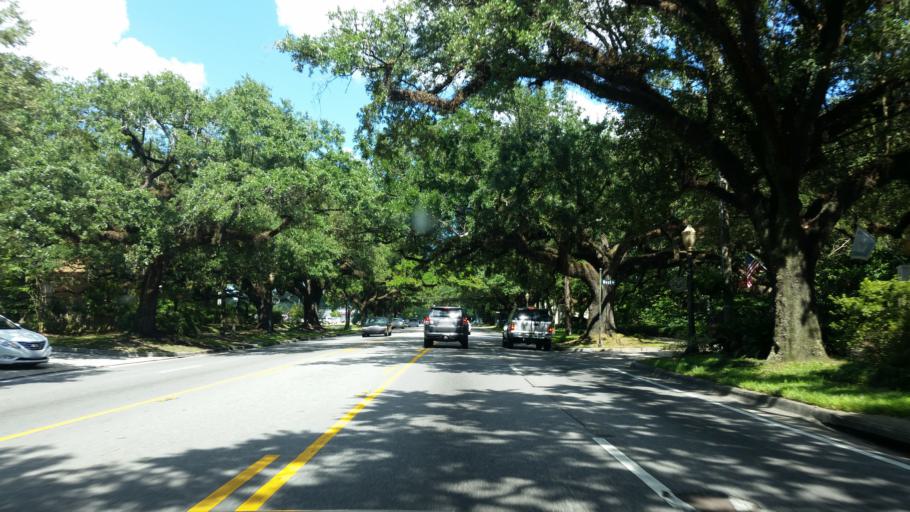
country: US
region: Alabama
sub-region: Mobile County
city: Mobile
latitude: 30.6792
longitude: -88.0766
